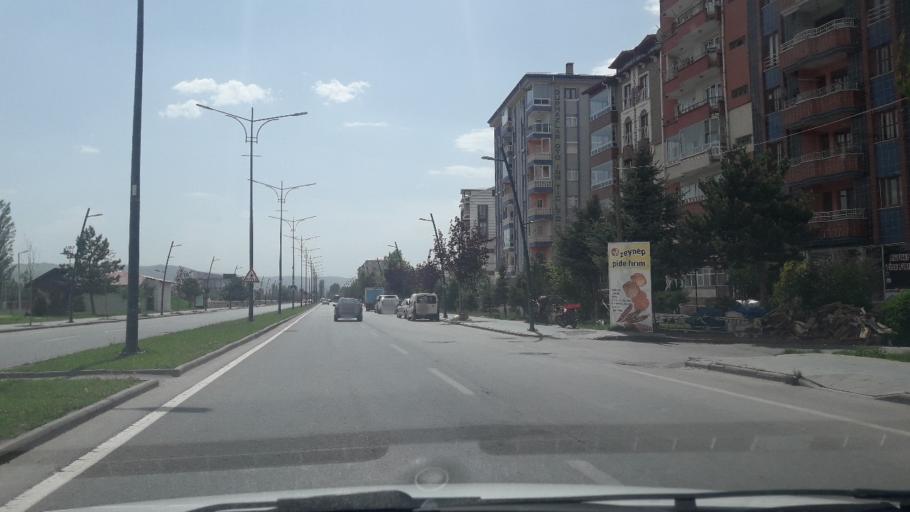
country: TR
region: Sivas
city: Sivas
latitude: 39.7300
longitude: 36.9807
